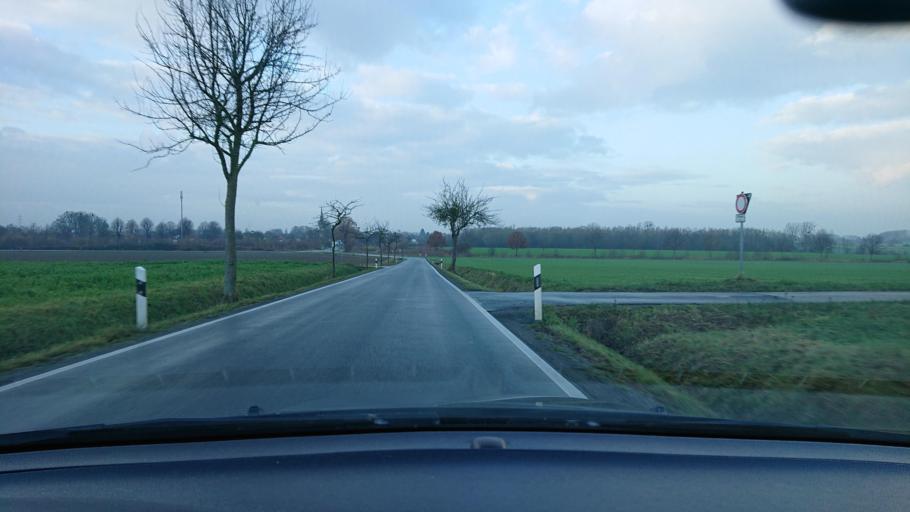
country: DE
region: North Rhine-Westphalia
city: Erwitte
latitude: 51.6157
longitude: 8.2584
